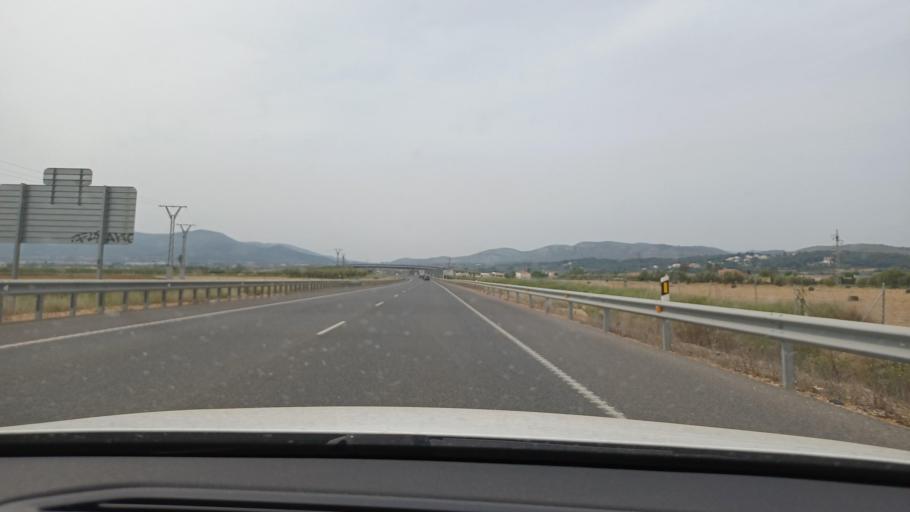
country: ES
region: Valencia
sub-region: Provincia de Castello
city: Benicarlo
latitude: 40.4263
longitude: 0.3973
